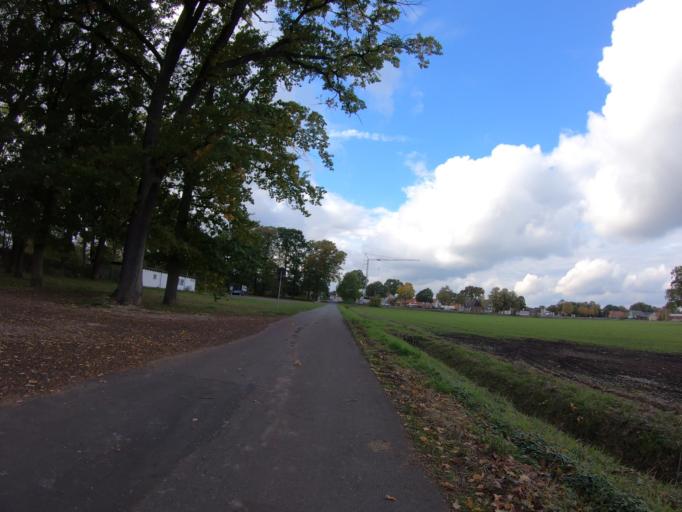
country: DE
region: Lower Saxony
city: Gifhorn
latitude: 52.5027
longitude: 10.5442
